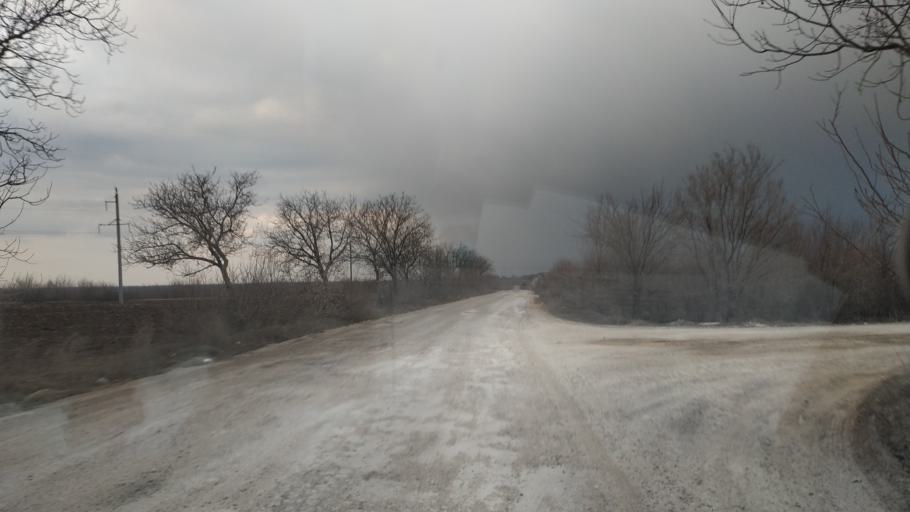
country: MD
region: Telenesti
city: Grigoriopol
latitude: 47.0546
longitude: 29.2940
